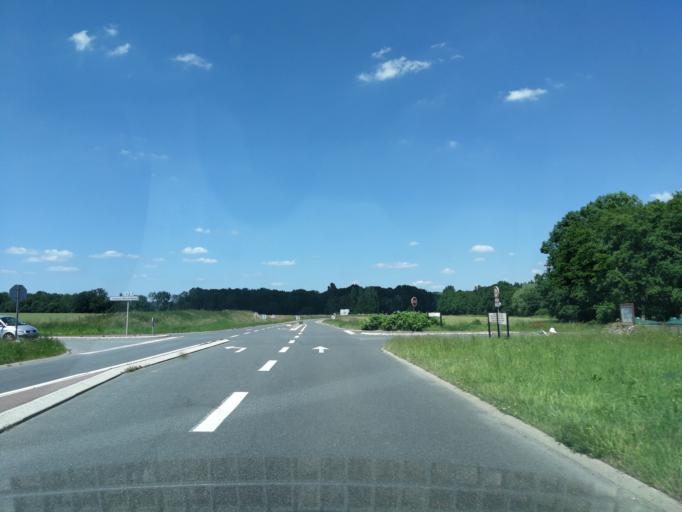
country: FR
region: Ile-de-France
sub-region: Departement de l'Essonne
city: Briis-sous-Forges
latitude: 48.6207
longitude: 2.1171
